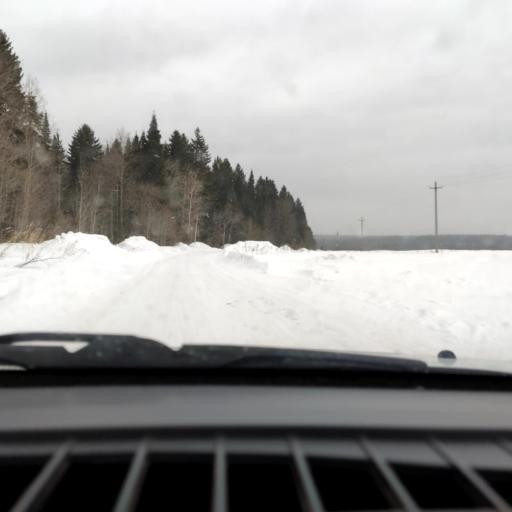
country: RU
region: Perm
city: Ferma
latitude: 57.9650
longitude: 56.3787
